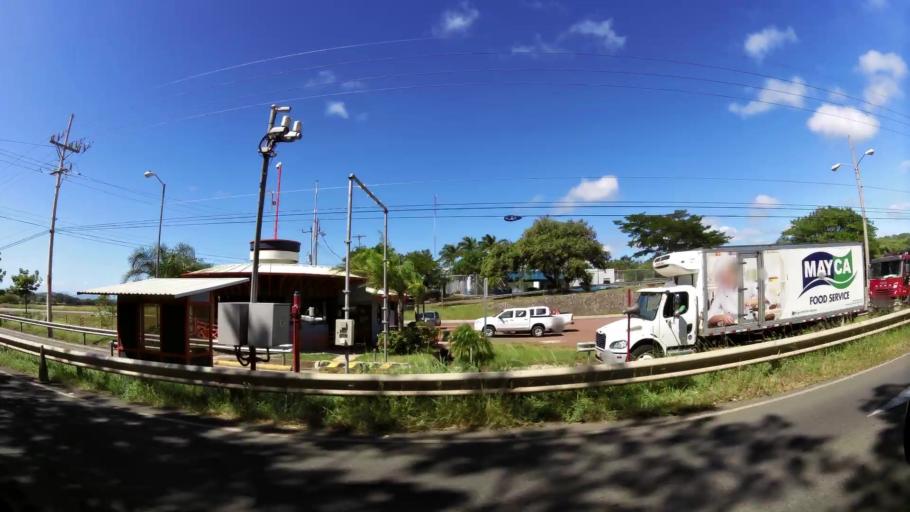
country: CR
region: Guanacaste
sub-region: Canton de Canas
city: Canas
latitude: 10.3899
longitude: -85.0813
